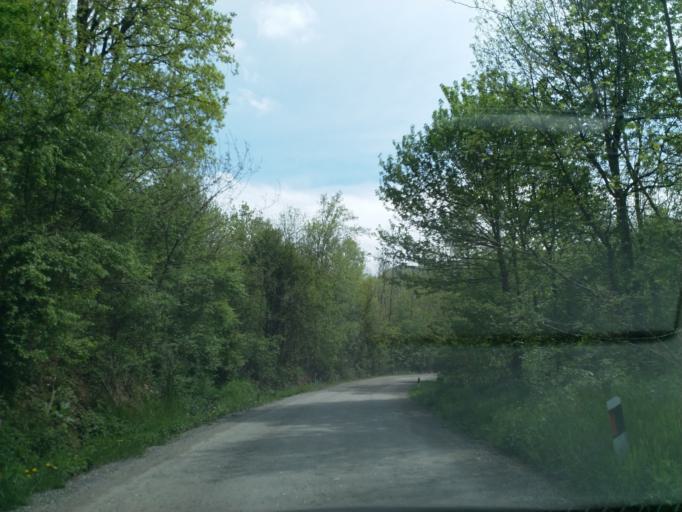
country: RS
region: Central Serbia
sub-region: Pomoravski Okrug
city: Despotovac
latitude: 43.9631
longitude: 21.5594
